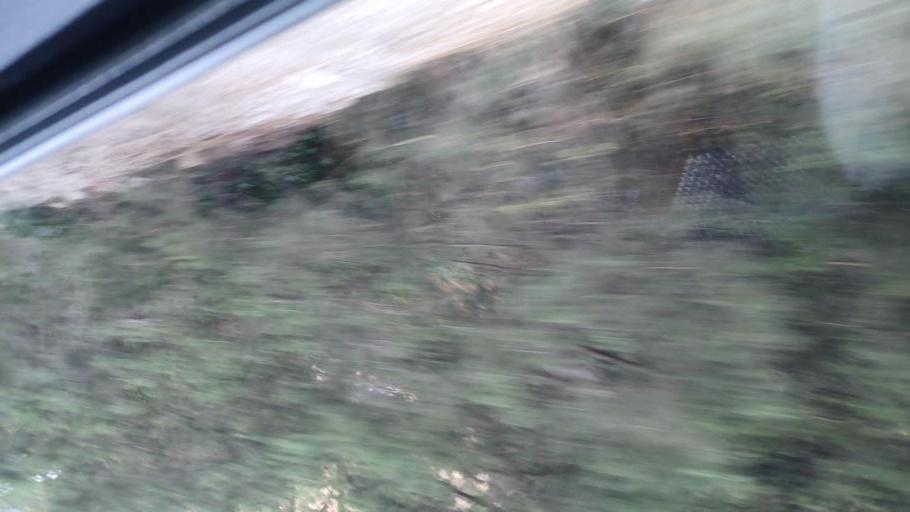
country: CY
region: Pafos
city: Tala
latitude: 34.8673
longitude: 32.4621
